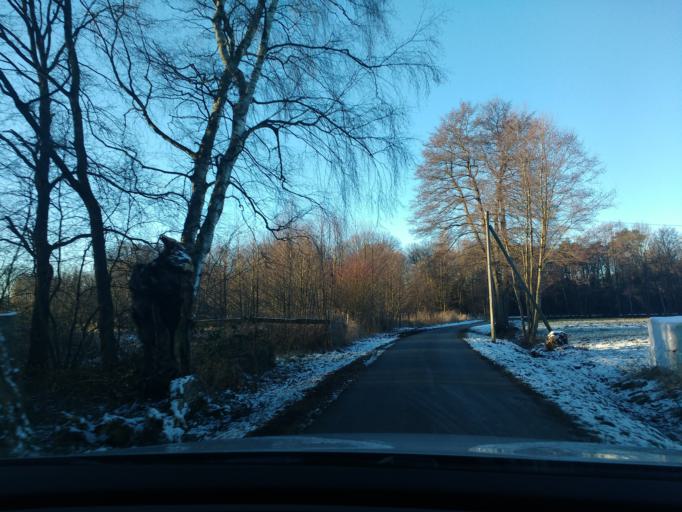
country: DE
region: North Rhine-Westphalia
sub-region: Regierungsbezirk Detmold
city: Paderborn
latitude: 51.7585
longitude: 8.7057
